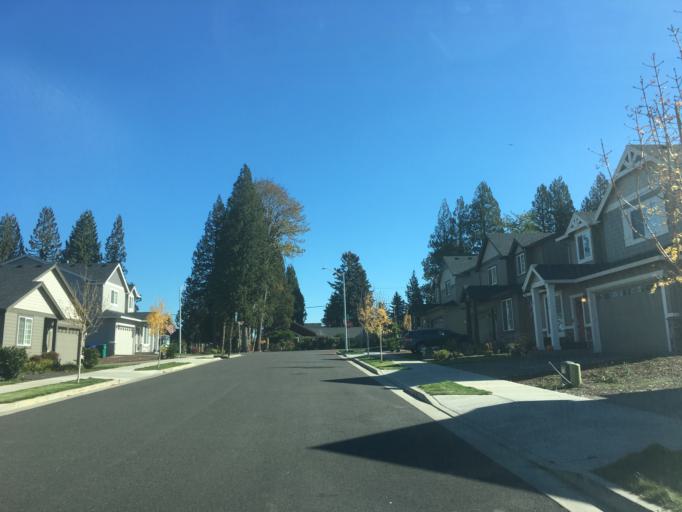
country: US
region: Oregon
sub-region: Multnomah County
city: Gresham
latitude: 45.4817
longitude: -122.4046
